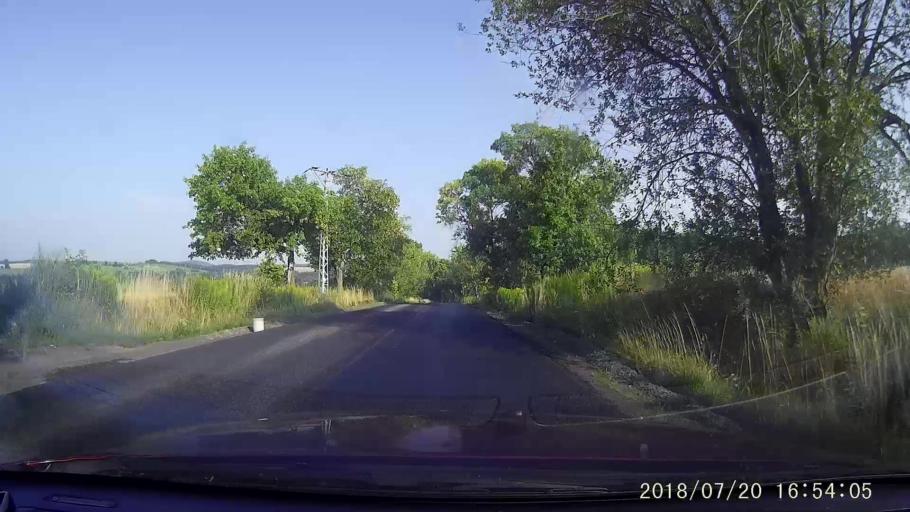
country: PL
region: Lower Silesian Voivodeship
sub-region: Powiat lubanski
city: Lesna
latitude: 51.0339
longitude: 15.2473
